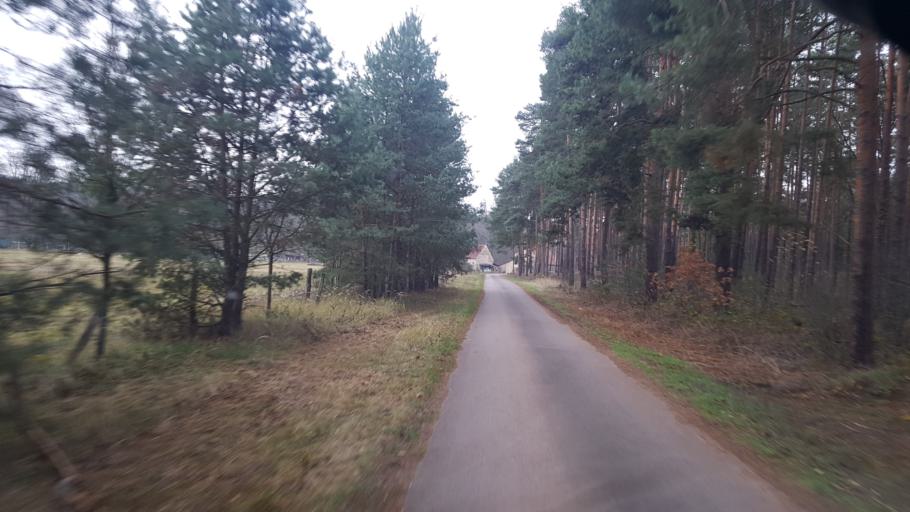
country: DE
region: Brandenburg
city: Schenkendobern
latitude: 51.9750
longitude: 14.6535
